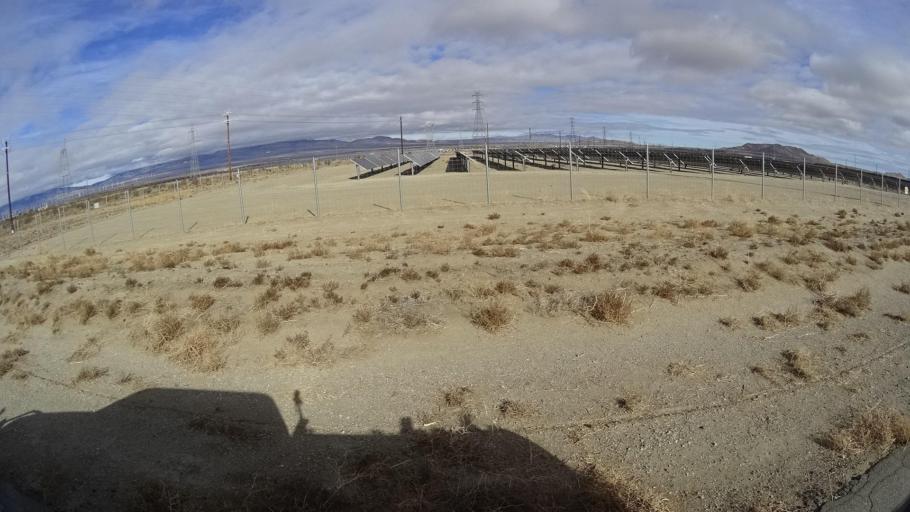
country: US
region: California
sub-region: Kern County
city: Rosamond
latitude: 34.8342
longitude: -118.3317
